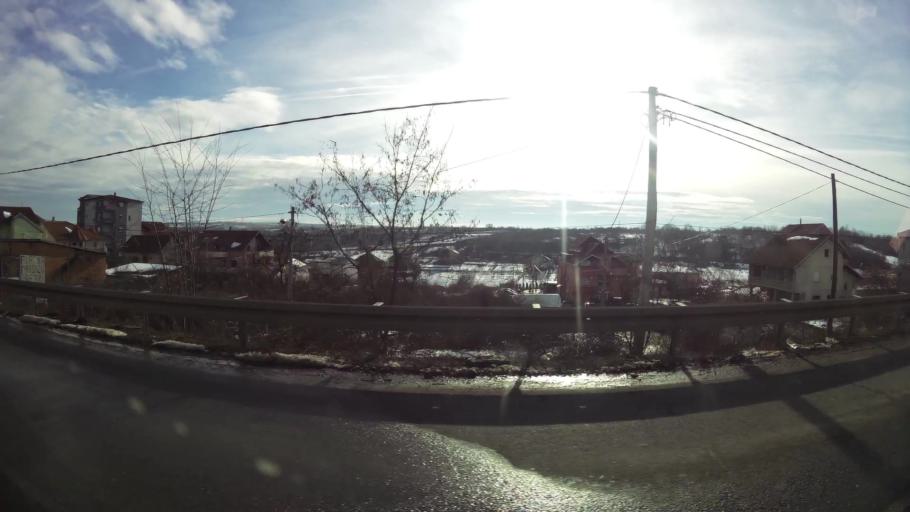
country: RS
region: Central Serbia
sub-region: Belgrade
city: Rakovica
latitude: 44.7179
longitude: 20.4229
